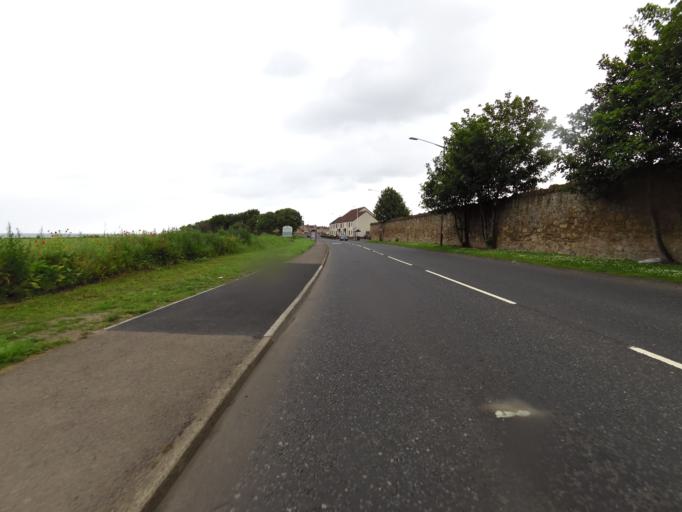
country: GB
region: Scotland
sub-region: East Lothian
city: Prestonpans
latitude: 55.9547
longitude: -2.9983
